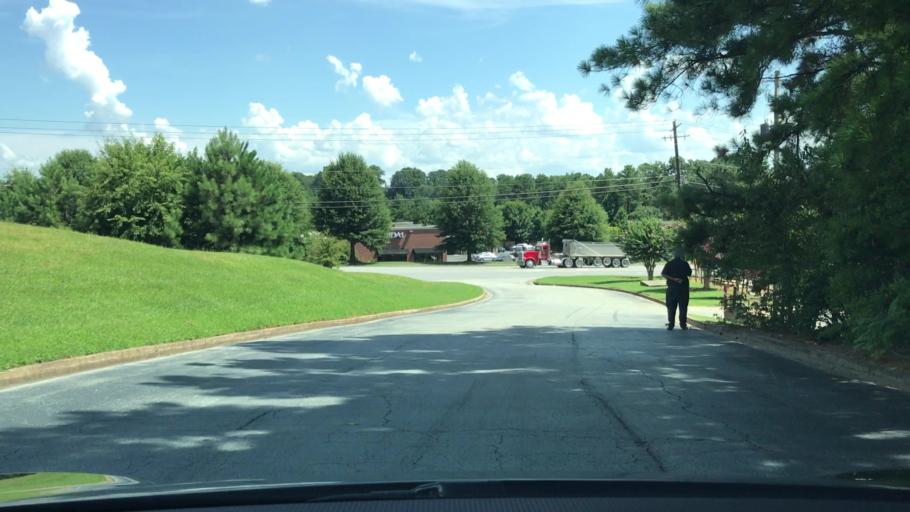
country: US
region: Georgia
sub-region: Gwinnett County
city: Sugar Hill
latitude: 34.0946
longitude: -84.0158
